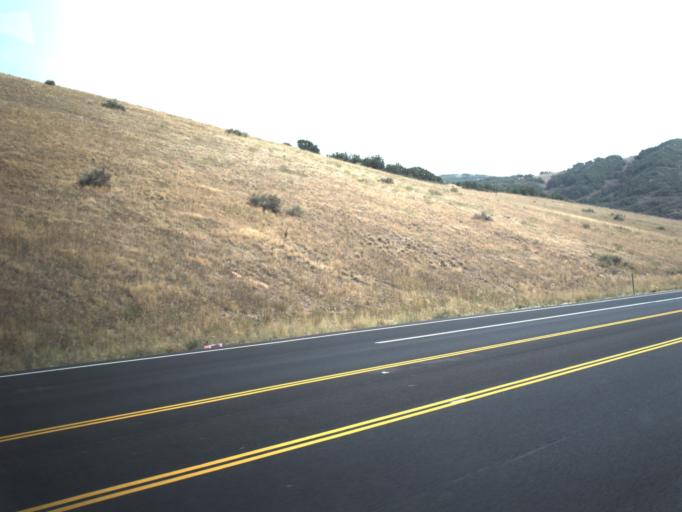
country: US
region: Utah
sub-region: Summit County
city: Park City
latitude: 40.6455
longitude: -111.4000
